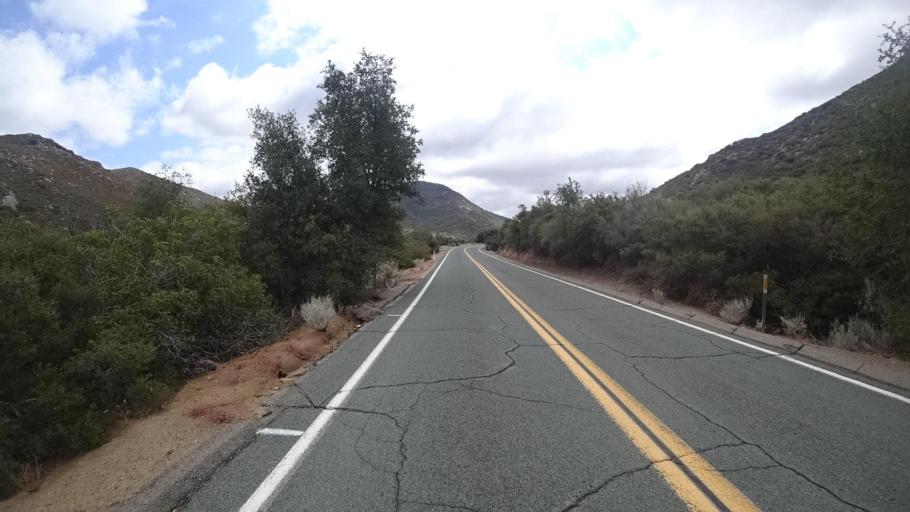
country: US
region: California
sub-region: San Diego County
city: Pine Valley
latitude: 32.7826
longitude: -116.4499
